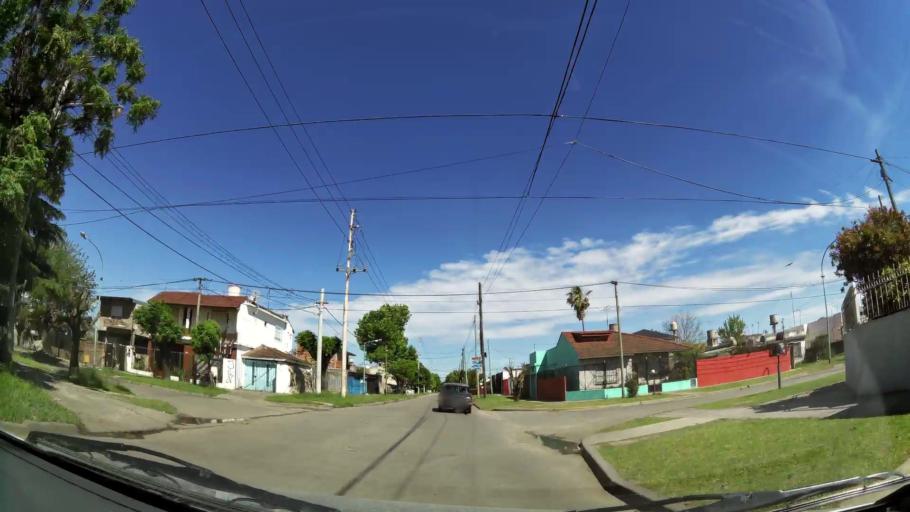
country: AR
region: Buenos Aires
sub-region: Partido de Almirante Brown
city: Adrogue
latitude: -34.7741
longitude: -58.3532
